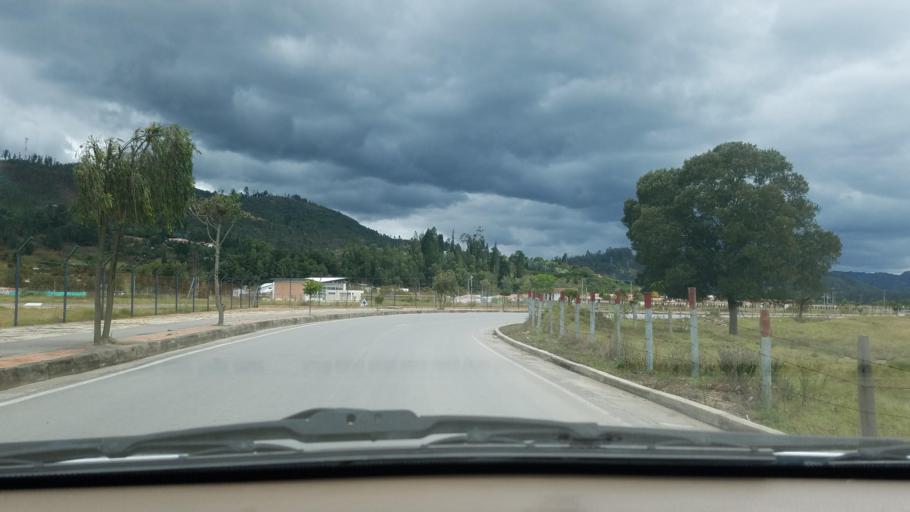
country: CO
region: Boyaca
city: Paipa
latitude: 5.7600
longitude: -73.1104
